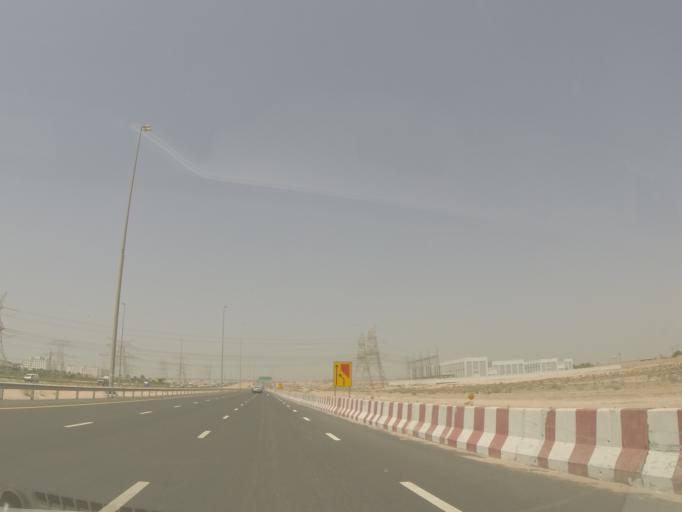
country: AE
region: Dubai
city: Dubai
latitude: 25.0073
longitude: 55.1707
